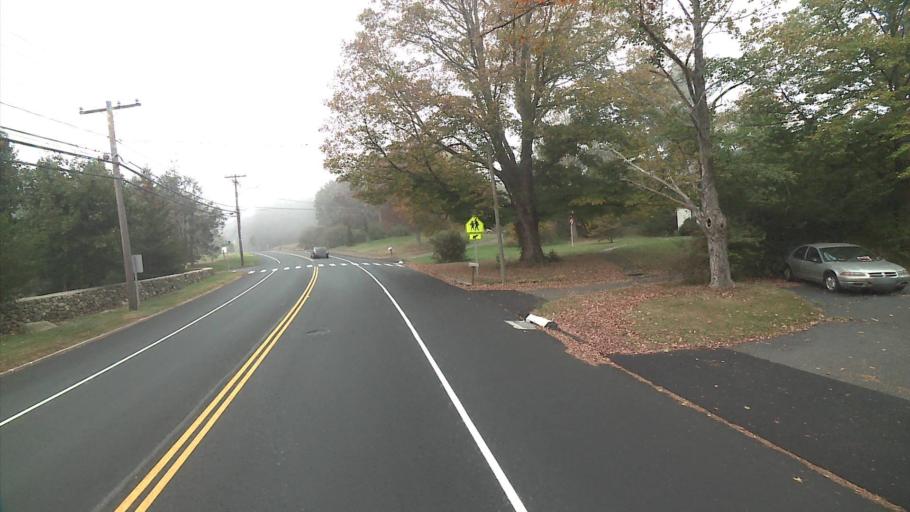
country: US
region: Connecticut
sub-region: Litchfield County
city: Watertown
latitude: 41.6043
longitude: -73.1309
